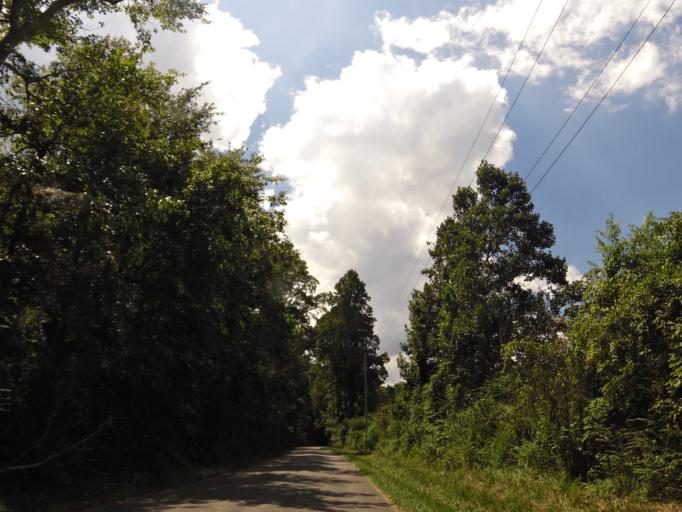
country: US
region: Tennessee
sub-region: Roane County
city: Rockwood
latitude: 35.8935
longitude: -84.7754
